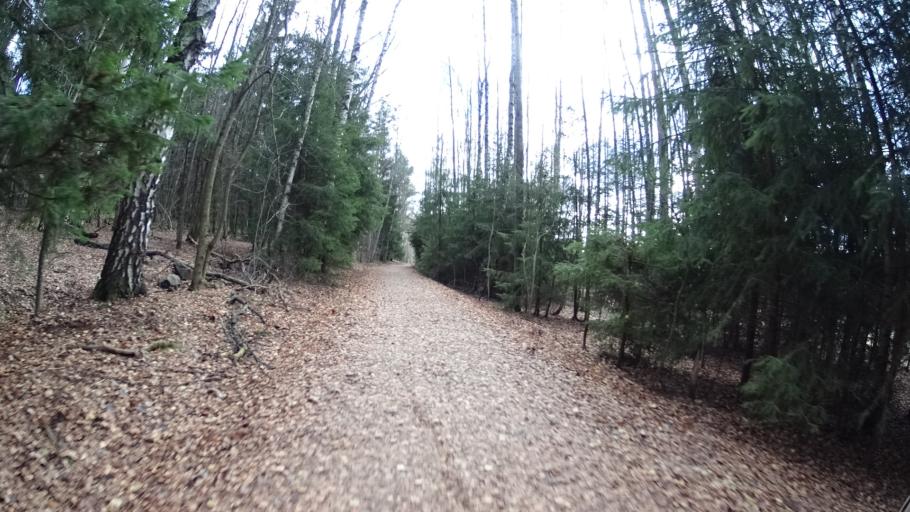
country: FI
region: Uusimaa
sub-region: Helsinki
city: Teekkarikylae
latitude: 60.2609
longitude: 24.8639
